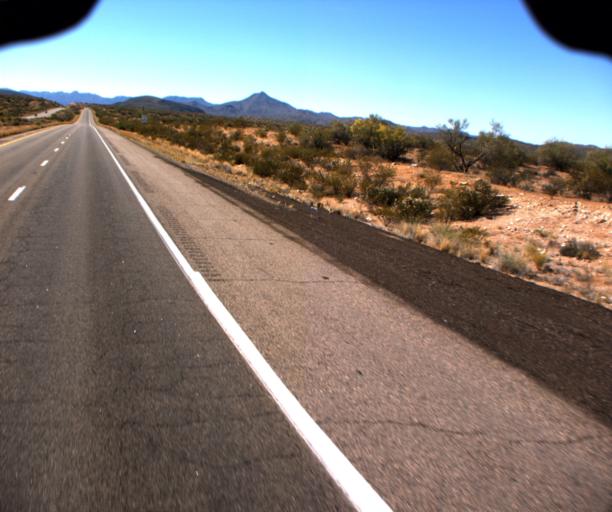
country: US
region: Arizona
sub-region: Yavapai County
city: Bagdad
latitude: 34.6092
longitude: -113.5243
